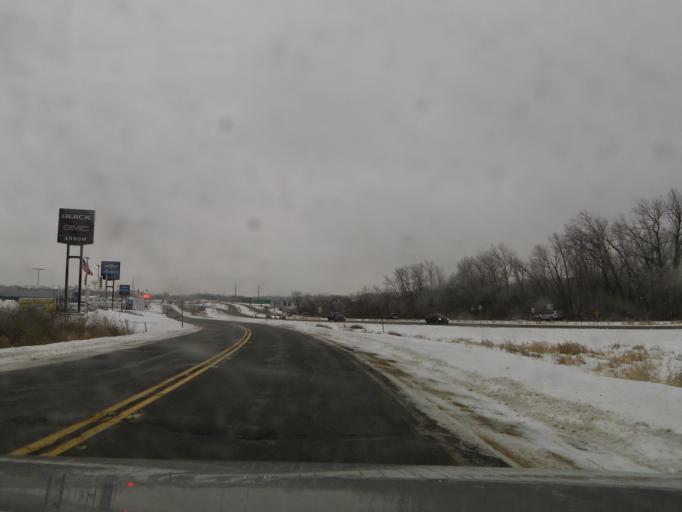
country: US
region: Minnesota
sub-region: Dakota County
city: West Saint Paul
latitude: 44.8822
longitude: -93.0893
